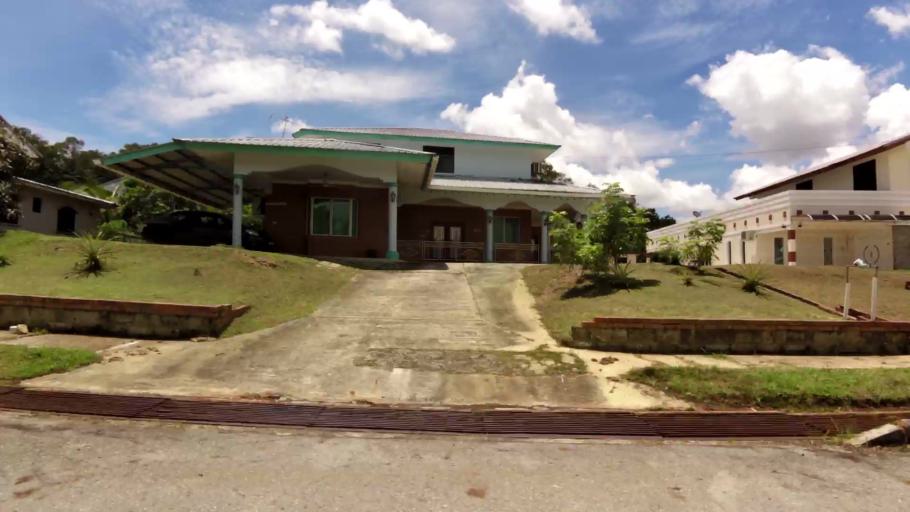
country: BN
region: Brunei and Muara
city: Bandar Seri Begawan
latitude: 4.9600
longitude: 114.9185
